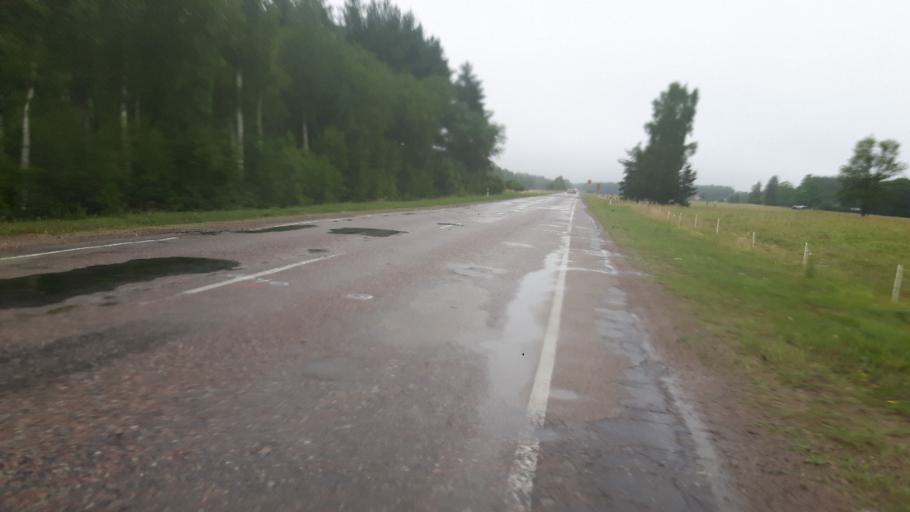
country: LT
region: Klaipedos apskritis
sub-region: Palanga
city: Sventoji
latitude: 56.0937
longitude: 21.1288
